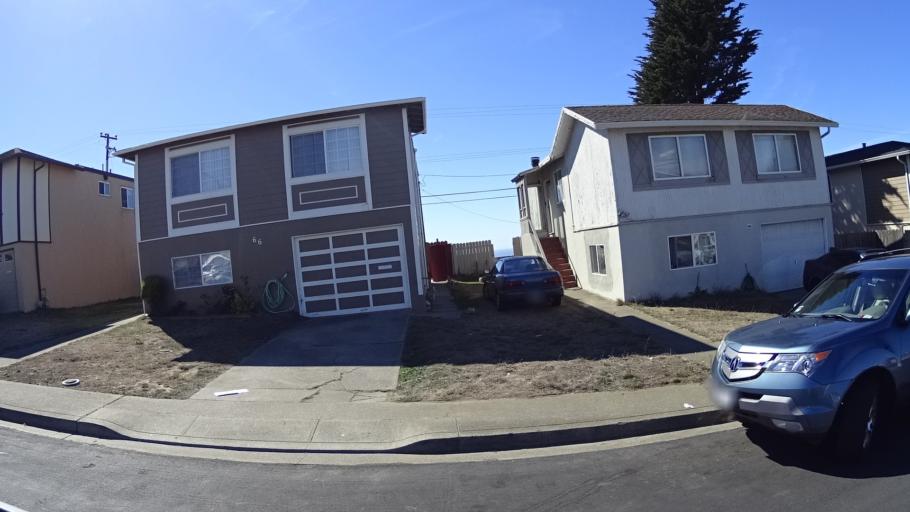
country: US
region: California
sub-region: San Mateo County
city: Broadmoor
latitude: 37.6725
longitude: -122.4900
